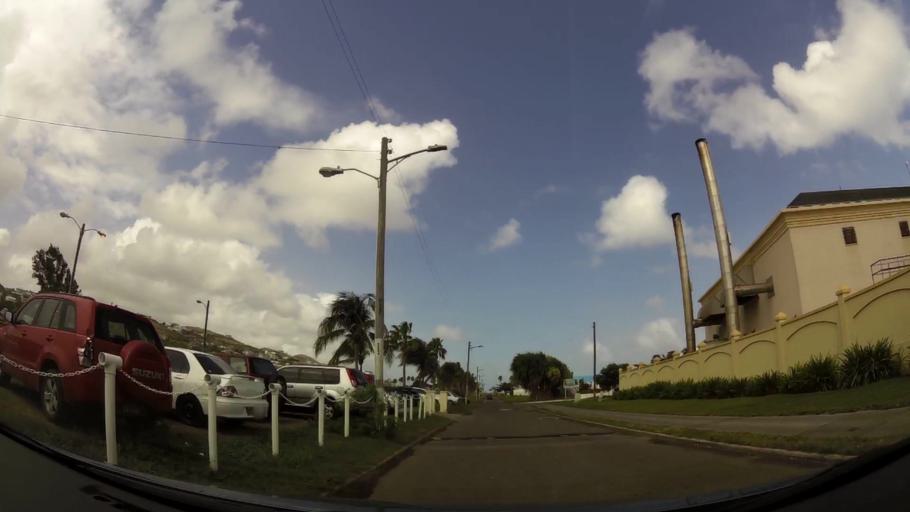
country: KN
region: Saint Peter Basseterre
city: Monkey Hill
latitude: 17.2937
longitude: -62.6862
